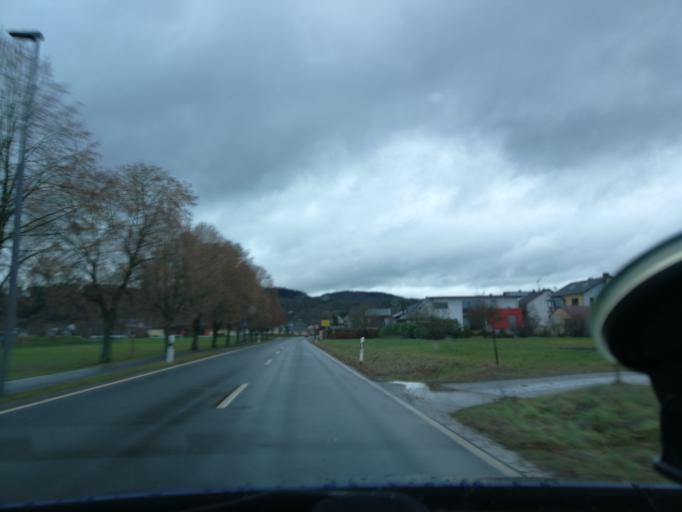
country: DE
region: Rheinland-Pfalz
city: Dreis
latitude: 49.9362
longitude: 6.8220
